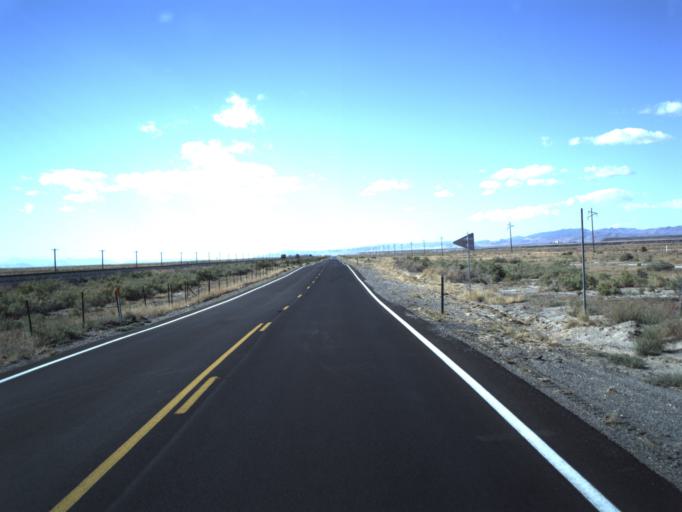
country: US
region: Utah
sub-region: Millard County
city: Delta
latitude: 39.2254
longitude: -112.6723
